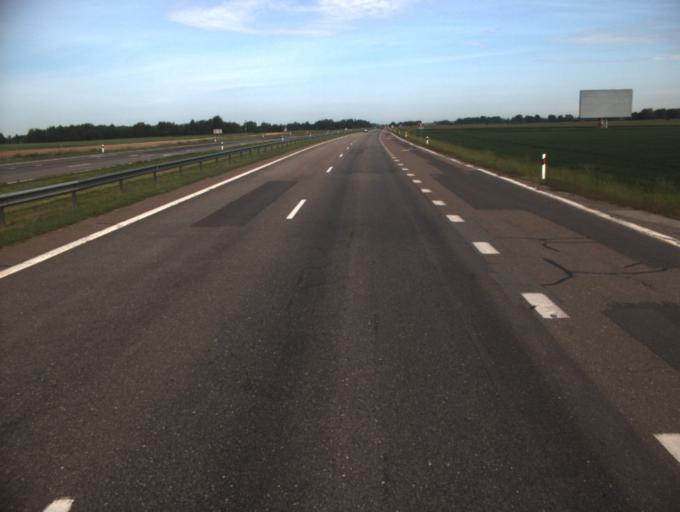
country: LT
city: Skaudvile
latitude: 55.4248
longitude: 22.7629
